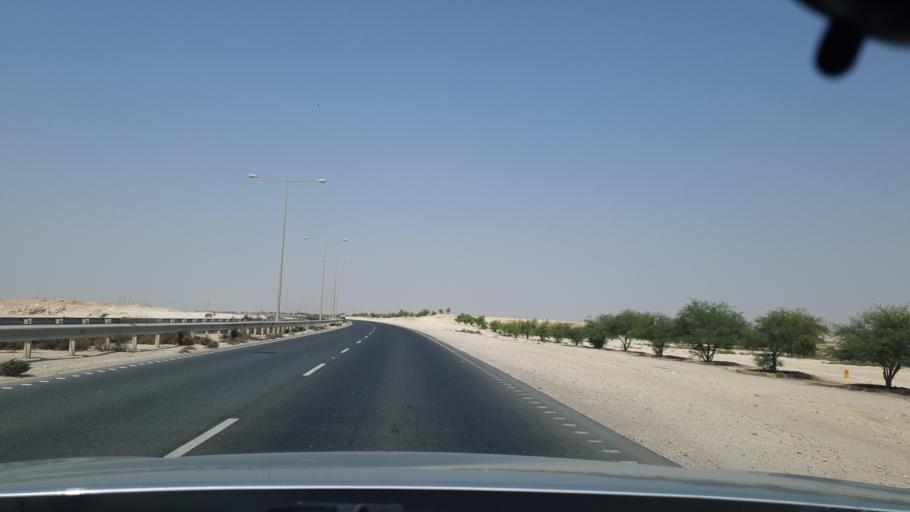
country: QA
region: Al Khawr
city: Al Khawr
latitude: 25.7327
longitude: 51.4938
